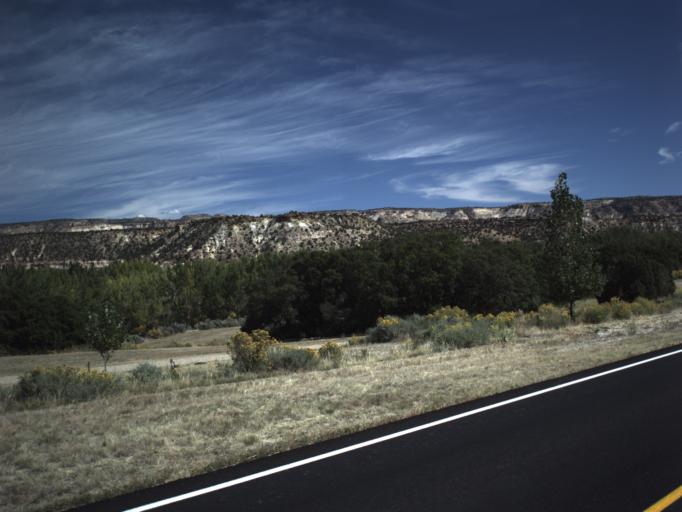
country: US
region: Utah
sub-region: Wayne County
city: Loa
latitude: 37.7758
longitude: -111.6383
